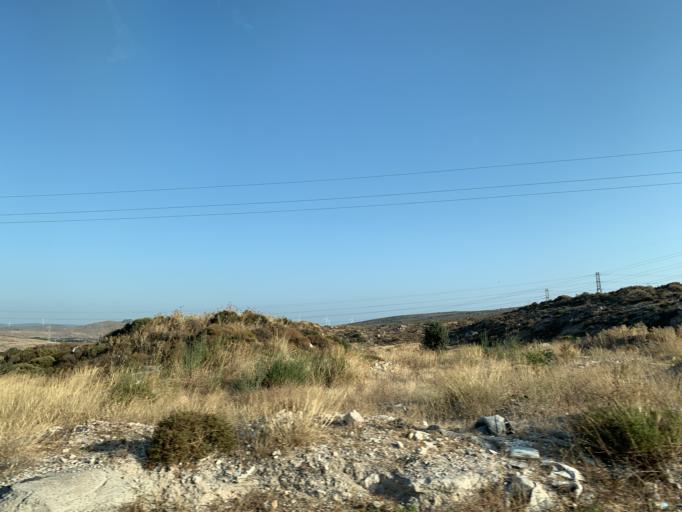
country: TR
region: Izmir
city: Alacati
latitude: 38.2768
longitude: 26.4187
